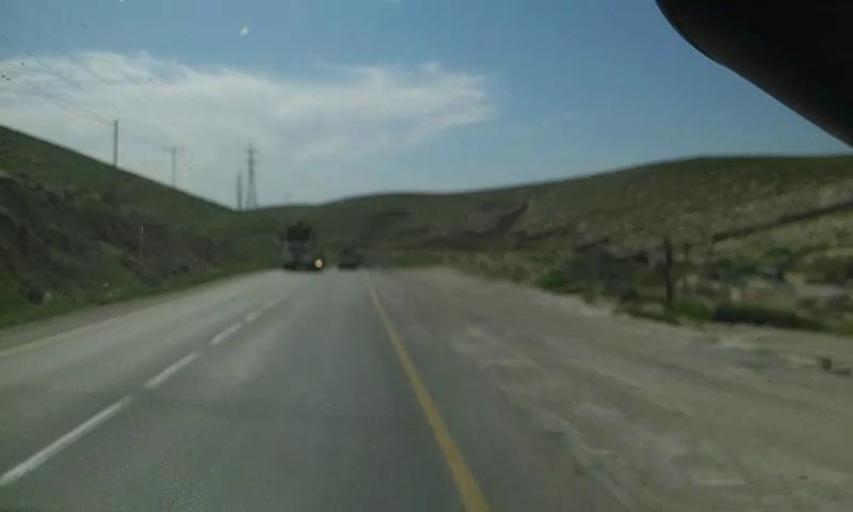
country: PS
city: Az Za`ayyim
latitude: 31.8097
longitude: 35.3066
